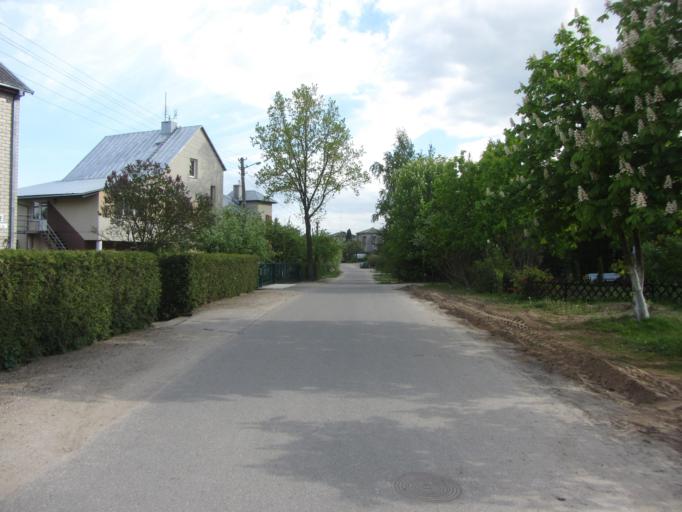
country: LT
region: Utenos apskritis
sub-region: Utena
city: Utena
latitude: 55.4890
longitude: 25.6025
